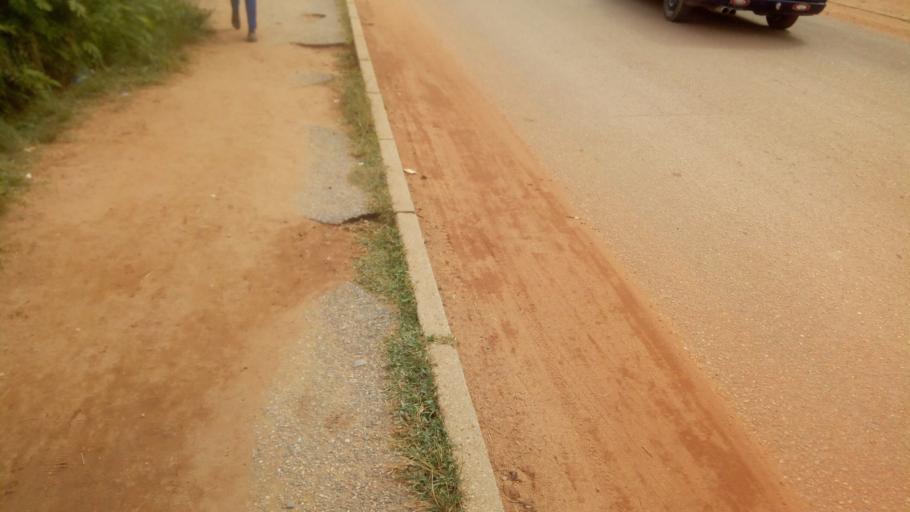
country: GH
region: Ashanti
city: Obuasi
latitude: 6.2114
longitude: -1.6868
